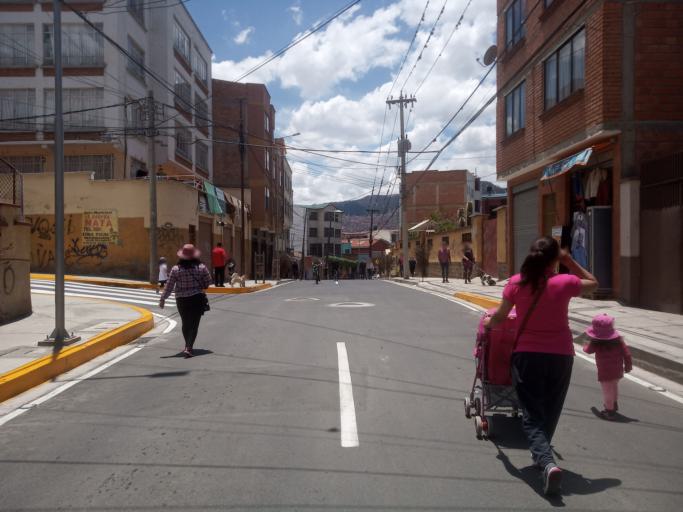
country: BO
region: La Paz
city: La Paz
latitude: -16.5104
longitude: -68.1346
